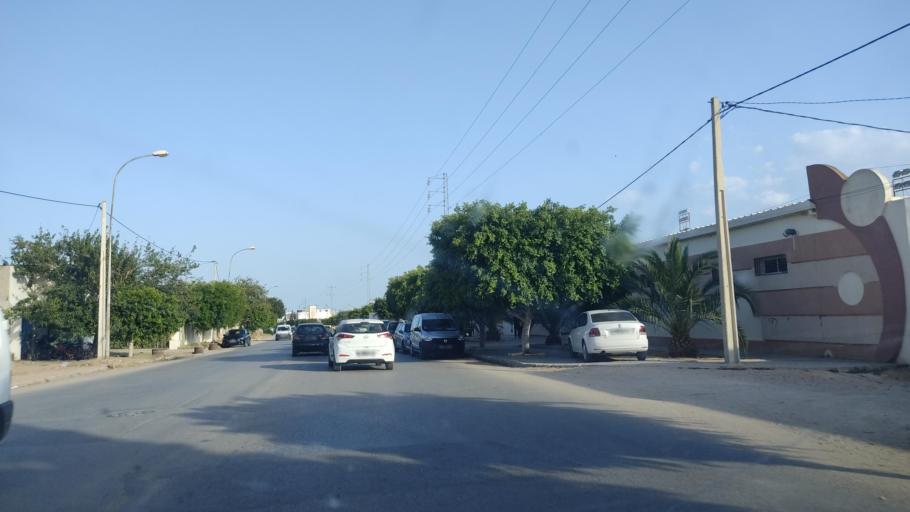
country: TN
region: Safaqis
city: Sfax
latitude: 34.7875
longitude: 10.6901
